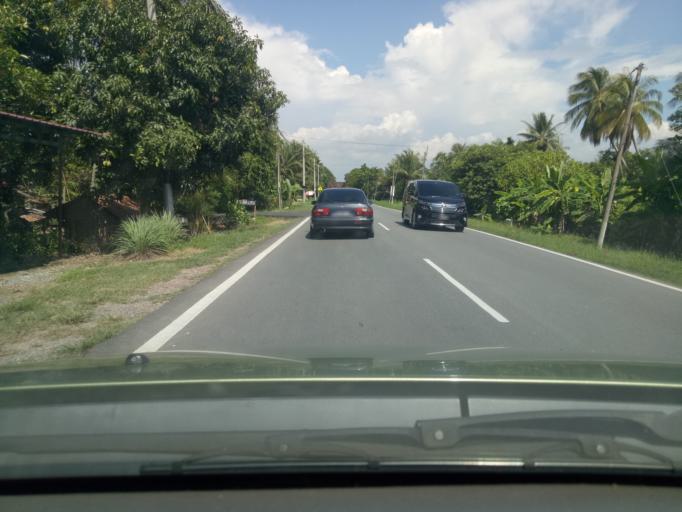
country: MY
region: Kedah
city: Alor Setar
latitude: 5.9712
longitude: 100.4174
